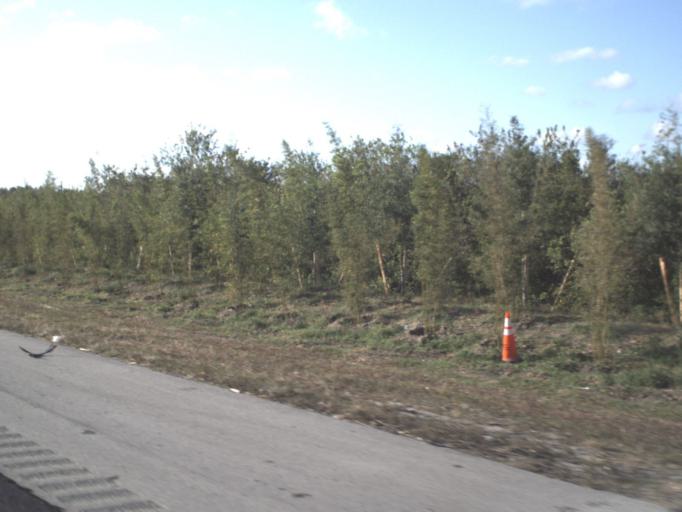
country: US
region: Florida
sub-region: Brevard County
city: Rockledge
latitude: 28.2986
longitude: -80.7523
